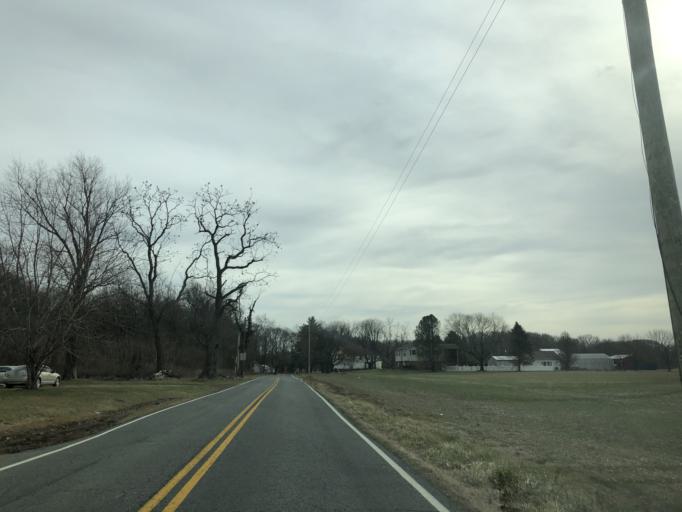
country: US
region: Delaware
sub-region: New Castle County
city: Middletown
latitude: 39.4180
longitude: -75.7729
